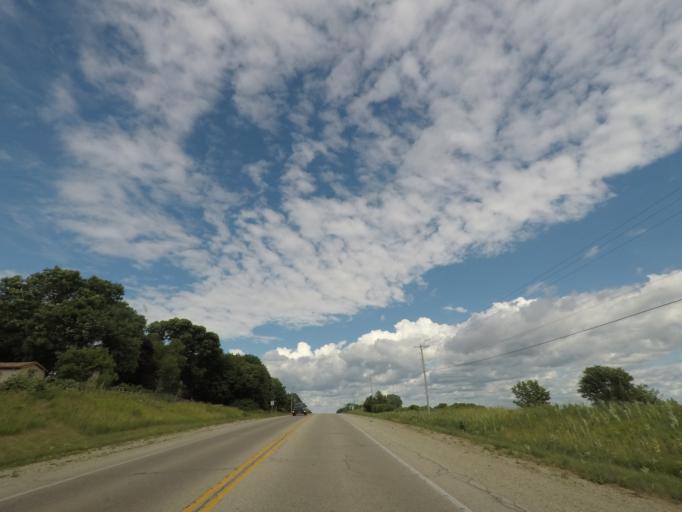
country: US
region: Wisconsin
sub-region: Rock County
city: Janesville
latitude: 42.6791
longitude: -89.0634
